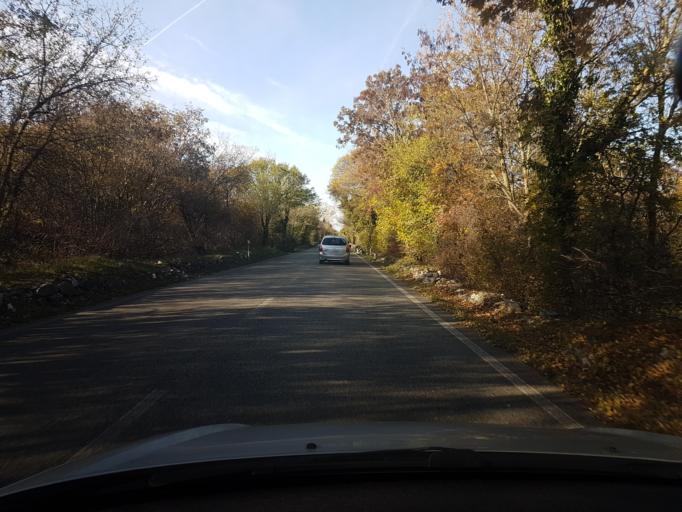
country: IT
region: Friuli Venezia Giulia
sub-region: Provincia di Trieste
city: Santa Croce
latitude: 45.7294
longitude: 13.7060
